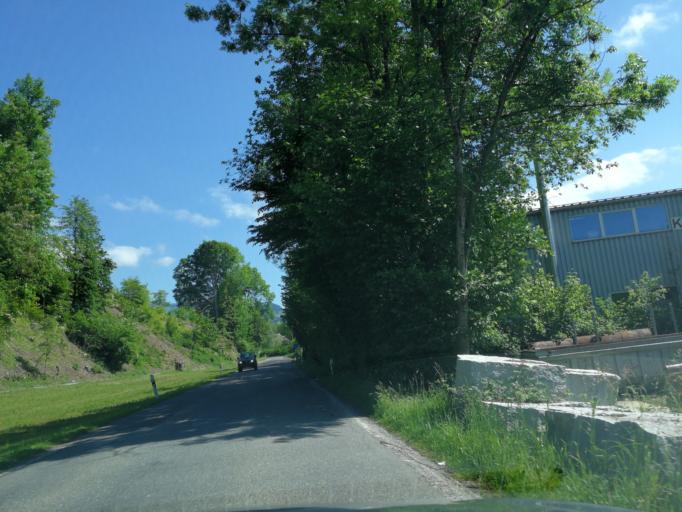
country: CH
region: Saint Gallen
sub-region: Wahlkreis See-Gaster
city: Eschenbach
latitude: 47.2341
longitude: 8.9250
